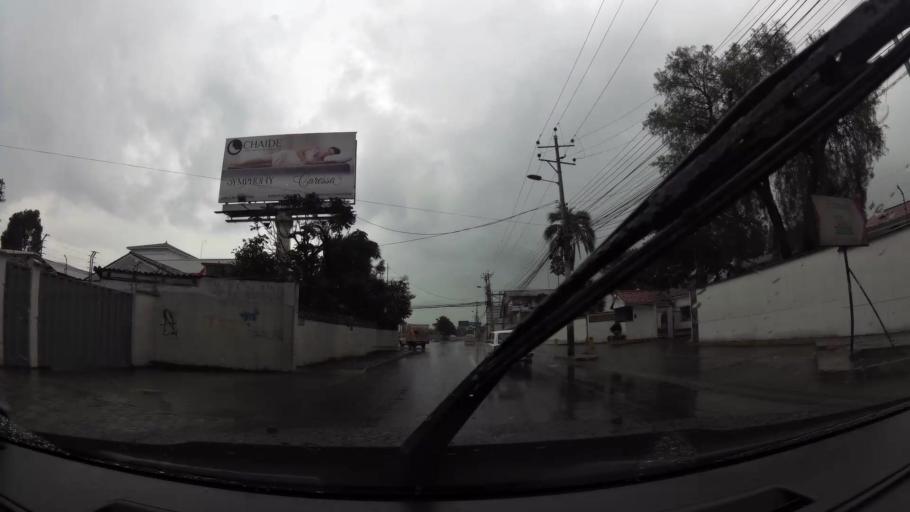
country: EC
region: Pichincha
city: Sangolqui
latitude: -0.3071
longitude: -78.4517
